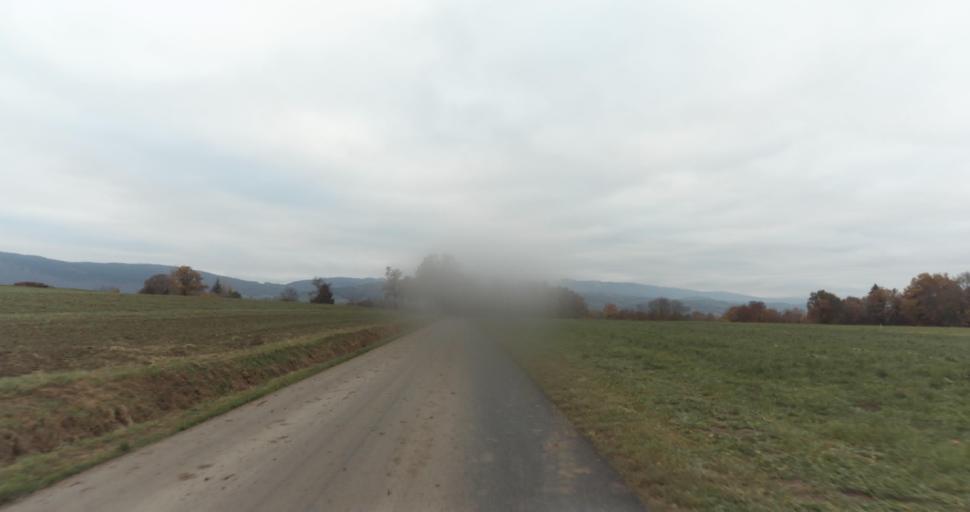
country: FR
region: Rhone-Alpes
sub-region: Departement de la Savoie
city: Albens
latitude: 45.7569
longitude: 5.9713
